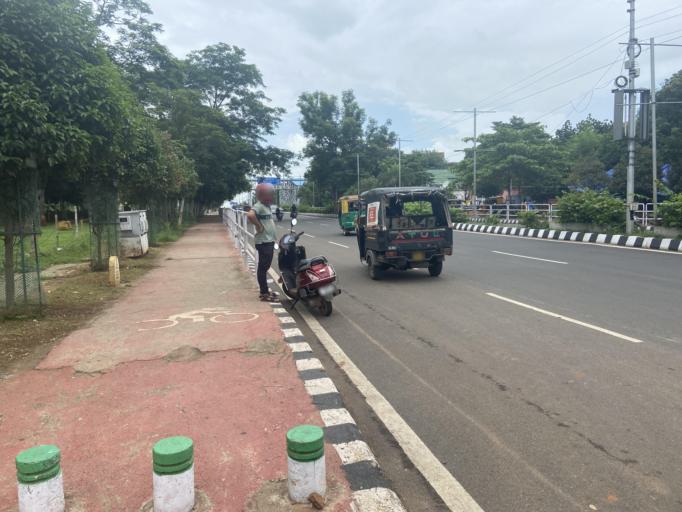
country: IN
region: Odisha
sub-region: Khordha
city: Bhubaneshwar
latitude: 20.2880
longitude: 85.8263
